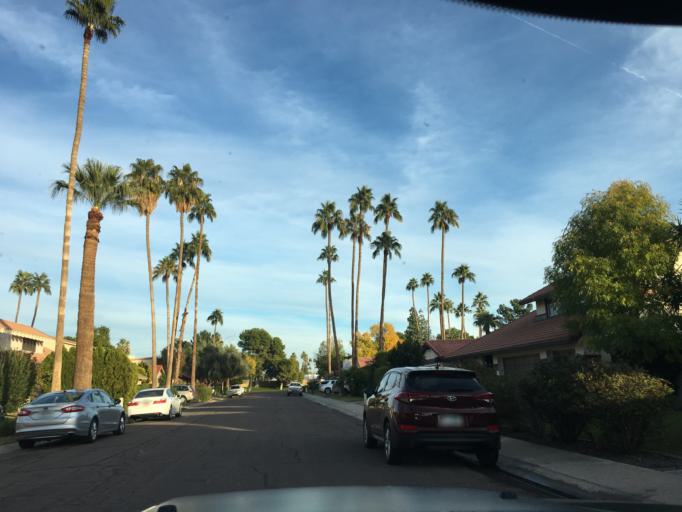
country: US
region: Arizona
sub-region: Maricopa County
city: Tempe
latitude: 33.3761
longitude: -111.9133
